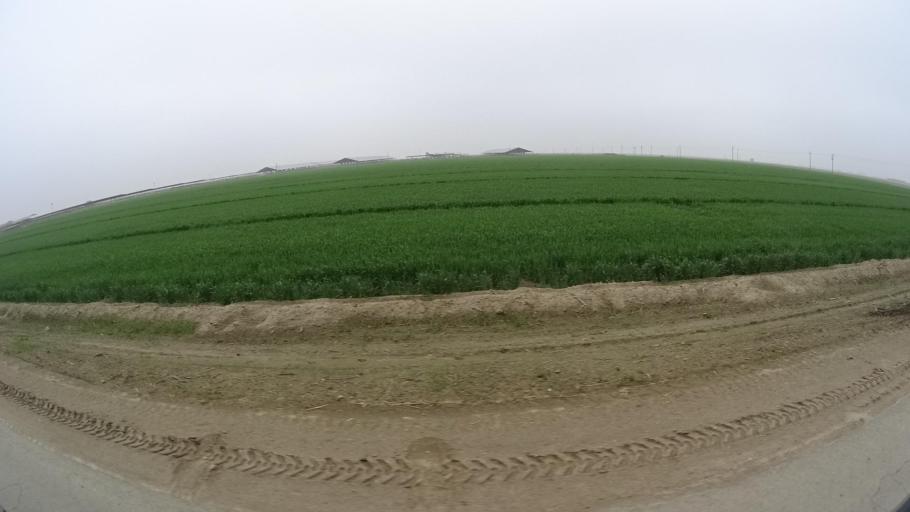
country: US
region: California
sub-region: Kern County
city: Wasco
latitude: 35.7157
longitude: -119.4194
